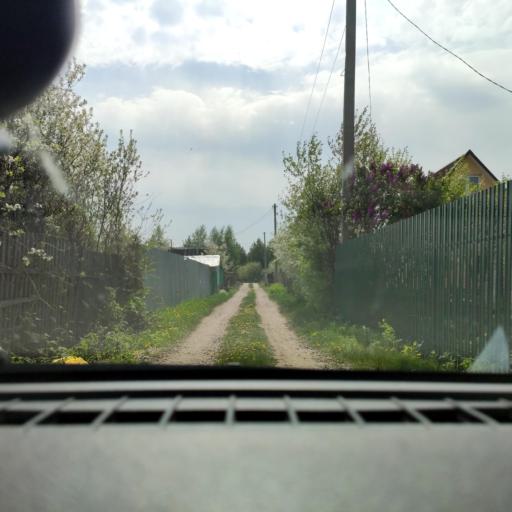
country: RU
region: Samara
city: Tol'yatti
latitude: 53.7060
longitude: 49.4128
